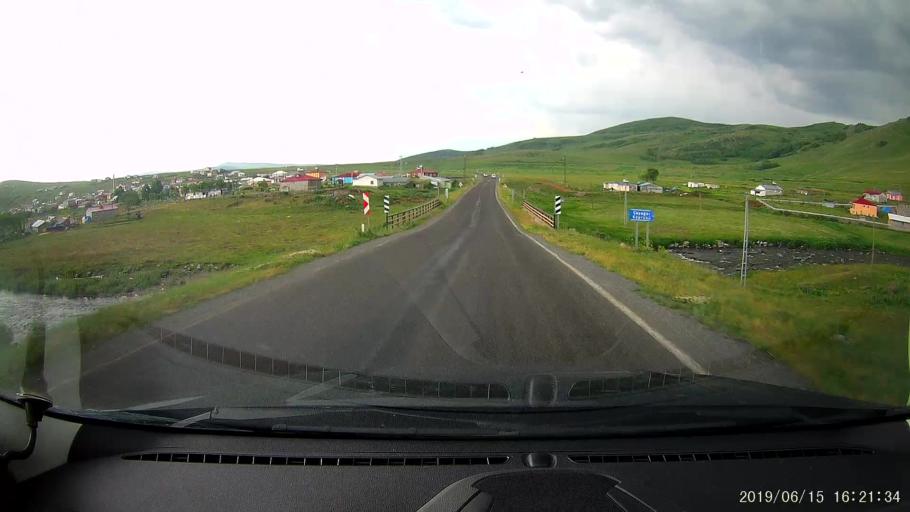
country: TR
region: Ardahan
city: Hanak
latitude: 41.1984
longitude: 42.8462
